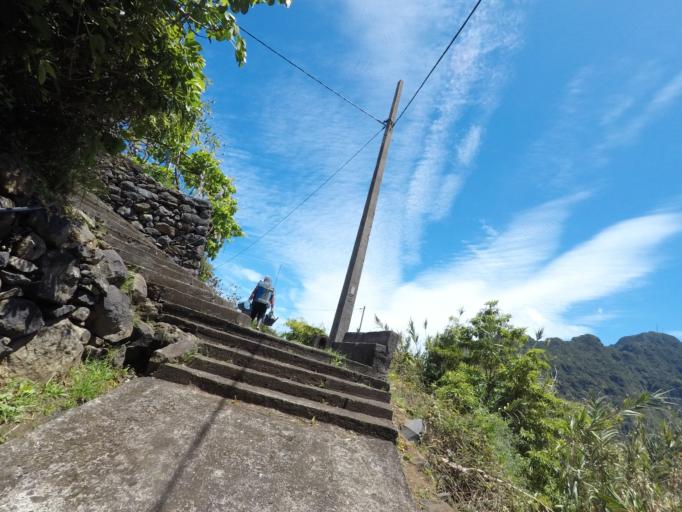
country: PT
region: Madeira
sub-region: Sao Vicente
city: Sao Vicente
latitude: 32.8247
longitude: -16.9784
